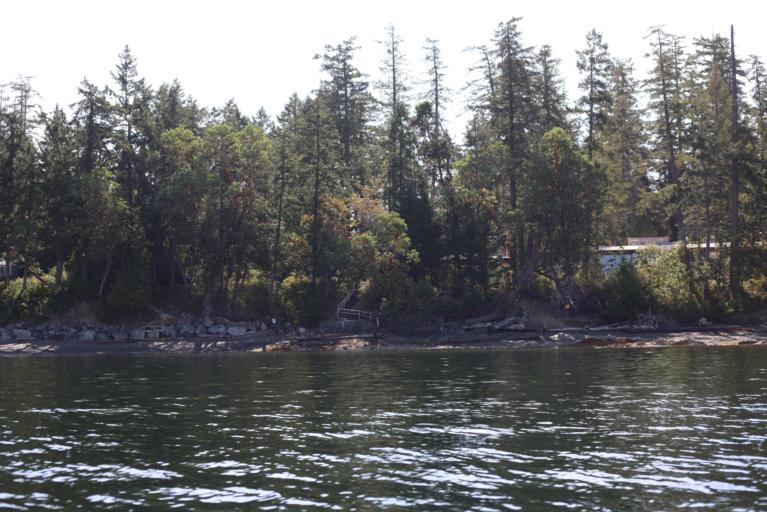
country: CA
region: British Columbia
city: North Saanich
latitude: 48.6343
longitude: -123.4785
